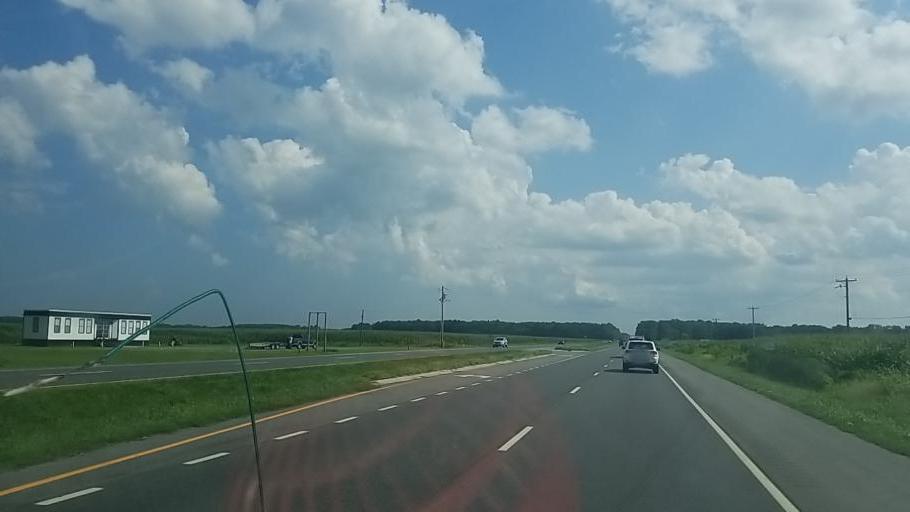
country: US
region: Delaware
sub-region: Sussex County
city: Selbyville
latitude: 38.4956
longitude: -75.2369
